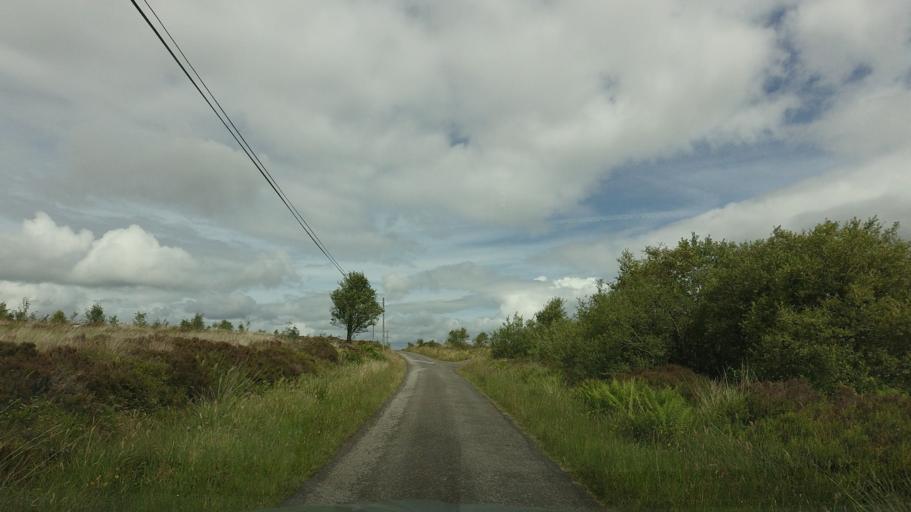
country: GB
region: Scotland
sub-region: Stirling
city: Killearn
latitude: 56.0885
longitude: -4.4351
